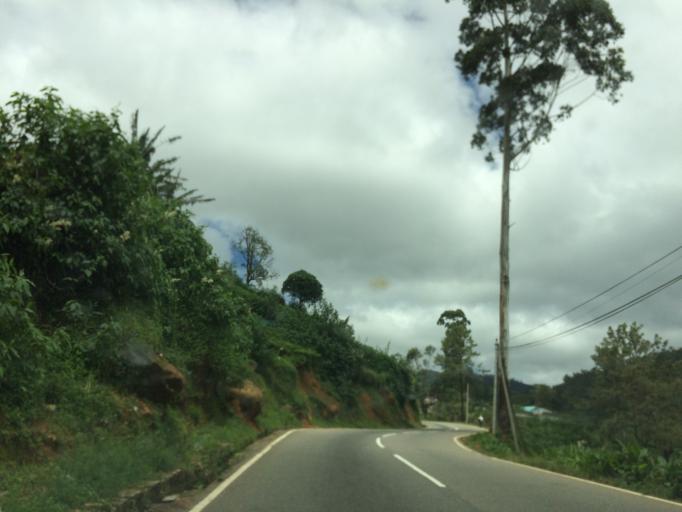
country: LK
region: Central
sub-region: Nuwara Eliya District
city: Nuwara Eliya
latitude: 7.0226
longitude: 80.7219
